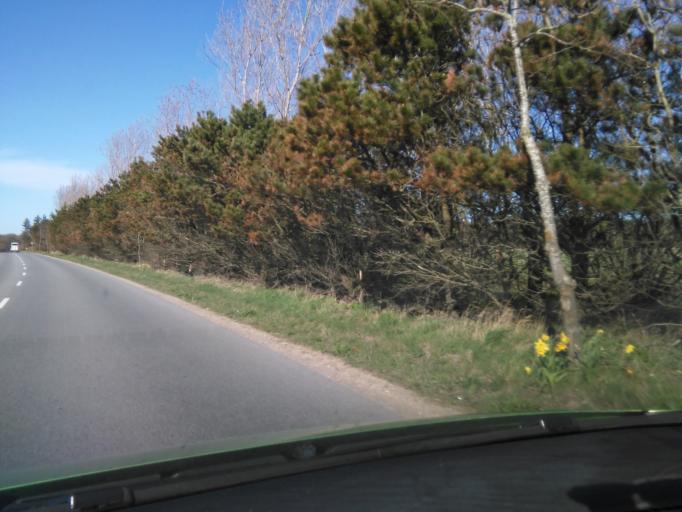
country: DK
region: South Denmark
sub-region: Varde Kommune
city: Oksbol
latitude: 55.6449
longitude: 8.2844
